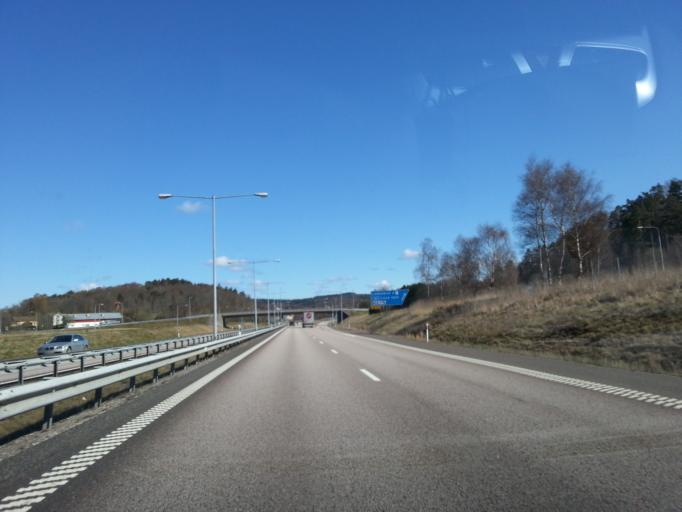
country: SE
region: Vaestra Goetaland
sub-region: Uddevalla Kommun
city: Ljungskile
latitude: 58.2109
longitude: 11.9132
